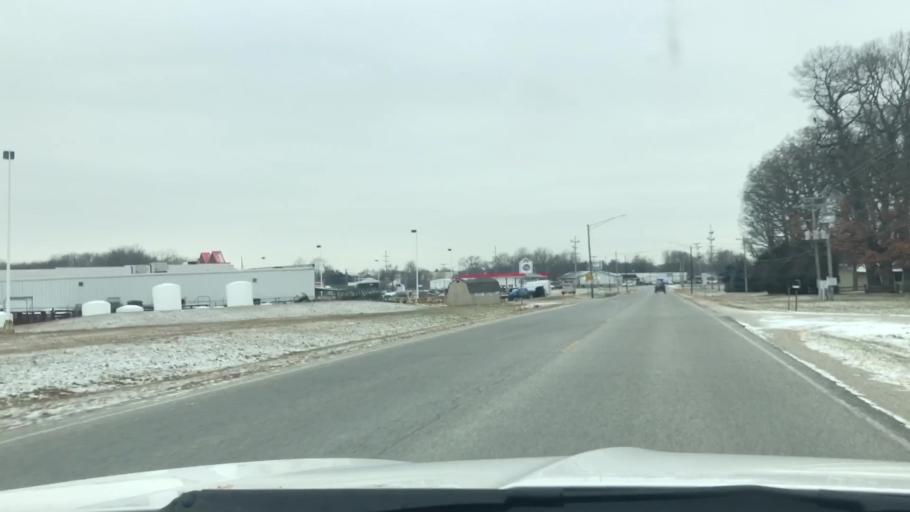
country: US
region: Indiana
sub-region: Fulton County
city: Rochester
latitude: 41.0533
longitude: -86.2141
